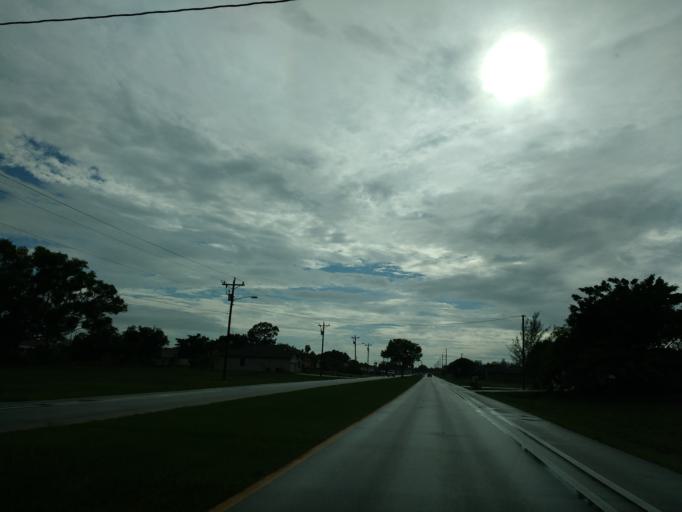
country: US
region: Florida
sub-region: Lee County
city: Cape Coral
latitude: 26.6228
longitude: -82.0111
